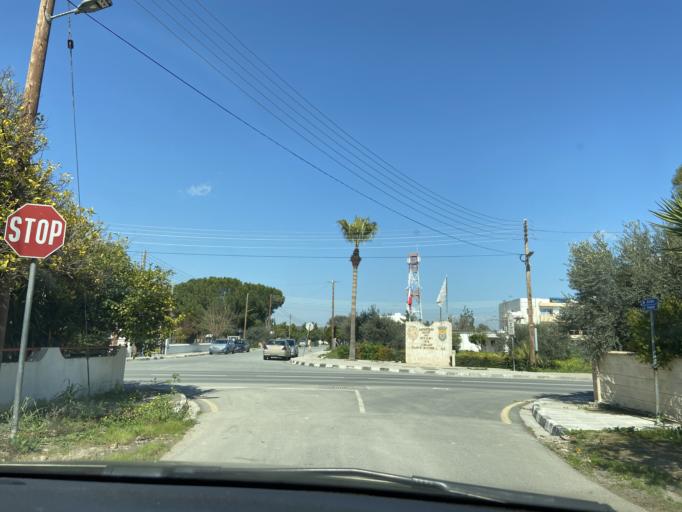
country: CY
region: Lefkosia
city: Dali
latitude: 35.0173
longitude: 33.4100
